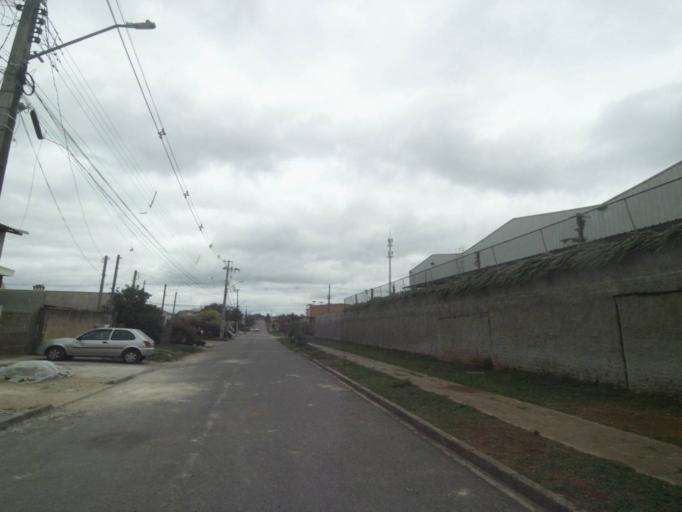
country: BR
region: Parana
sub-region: Sao Jose Dos Pinhais
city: Sao Jose dos Pinhais
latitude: -25.5562
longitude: -49.2683
